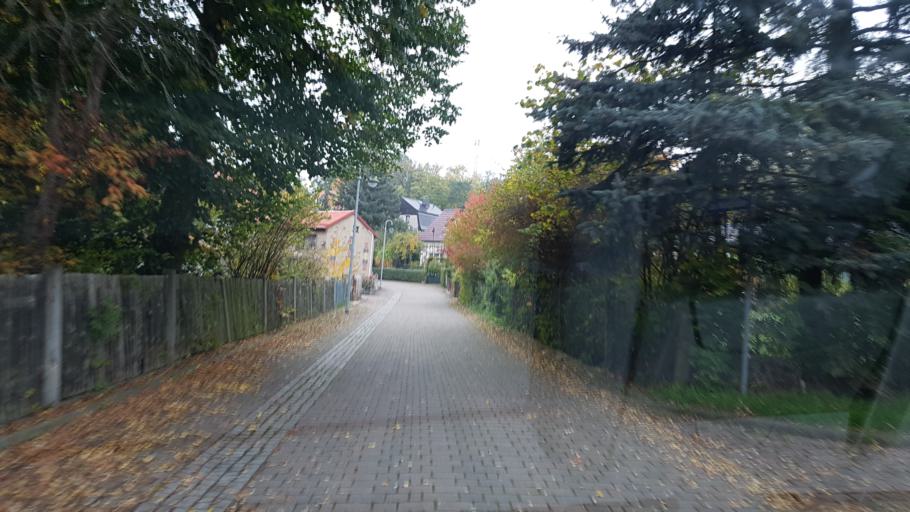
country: DE
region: Saxony
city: Dahlen
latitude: 51.3981
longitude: 12.9902
